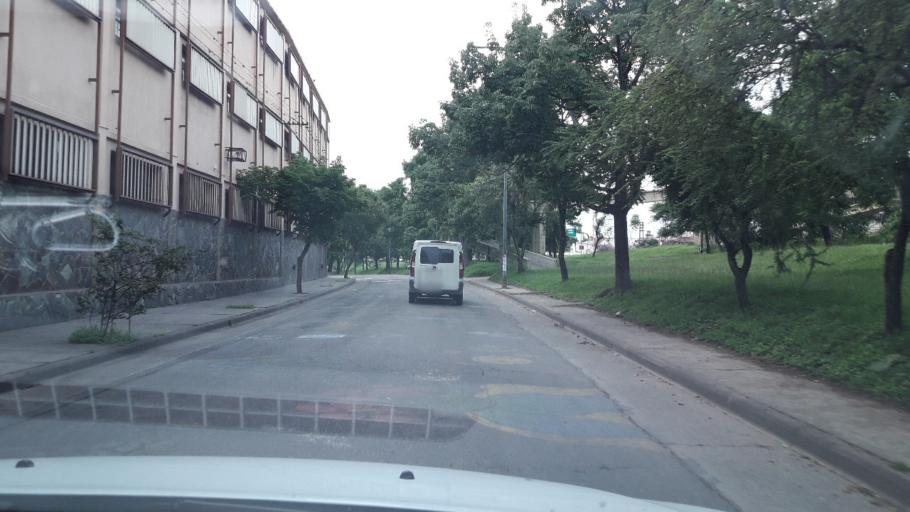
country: AR
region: Jujuy
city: San Salvador de Jujuy
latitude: -24.1933
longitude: -65.2926
